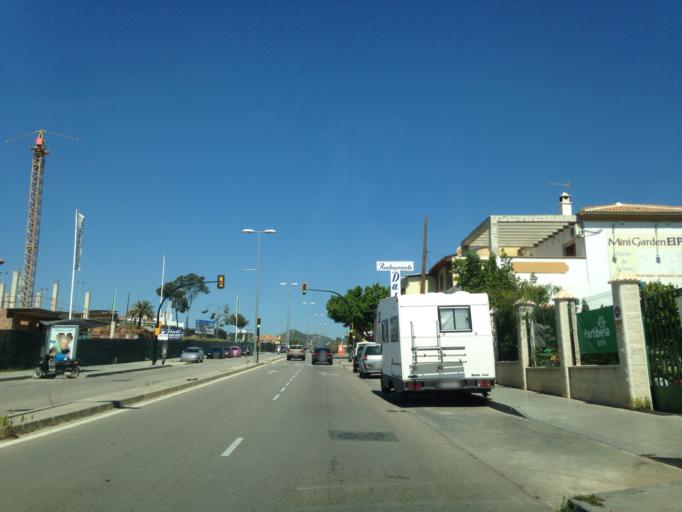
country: ES
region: Andalusia
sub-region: Provincia de Malaga
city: Malaga
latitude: 36.7409
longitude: -4.4872
